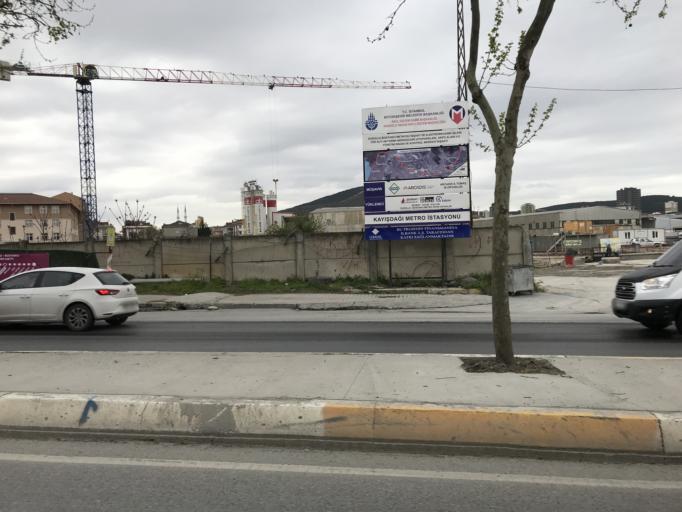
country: TR
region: Istanbul
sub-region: Atasehir
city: Atasehir
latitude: 40.9849
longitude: 29.1370
